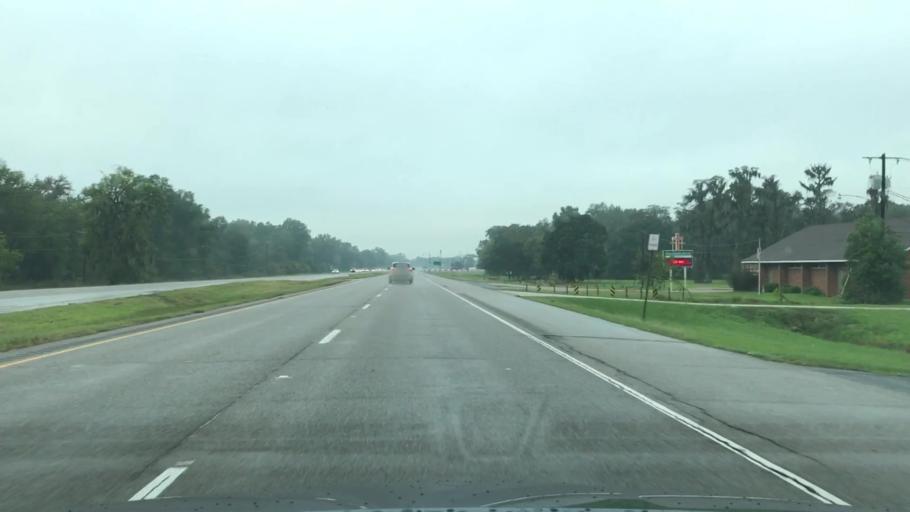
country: US
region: Louisiana
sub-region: Saint Charles Parish
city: Des Allemands
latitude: 29.8293
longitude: -90.4584
